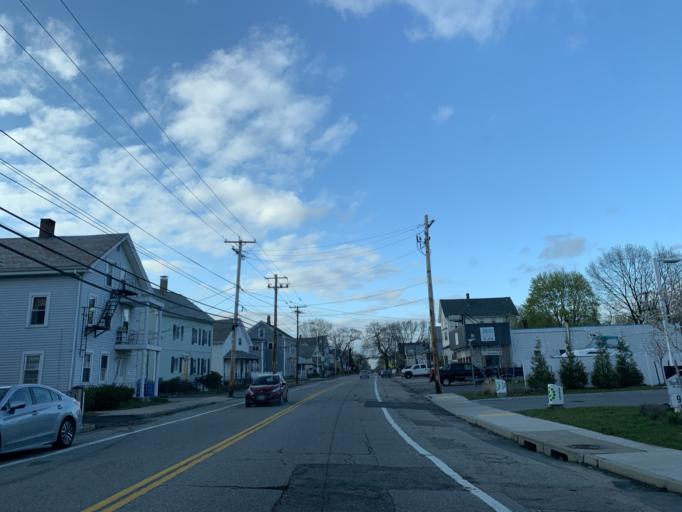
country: US
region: Rhode Island
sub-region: Providence County
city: Central Falls
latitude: 41.8812
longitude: -71.4157
